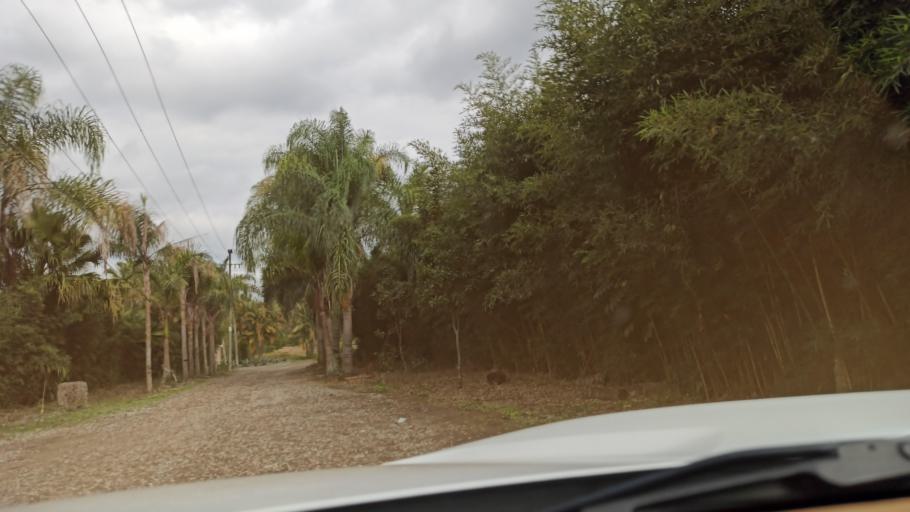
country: MX
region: Veracruz
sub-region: Fortin
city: Fortin de las Flores
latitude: 18.9023
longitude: -96.9922
